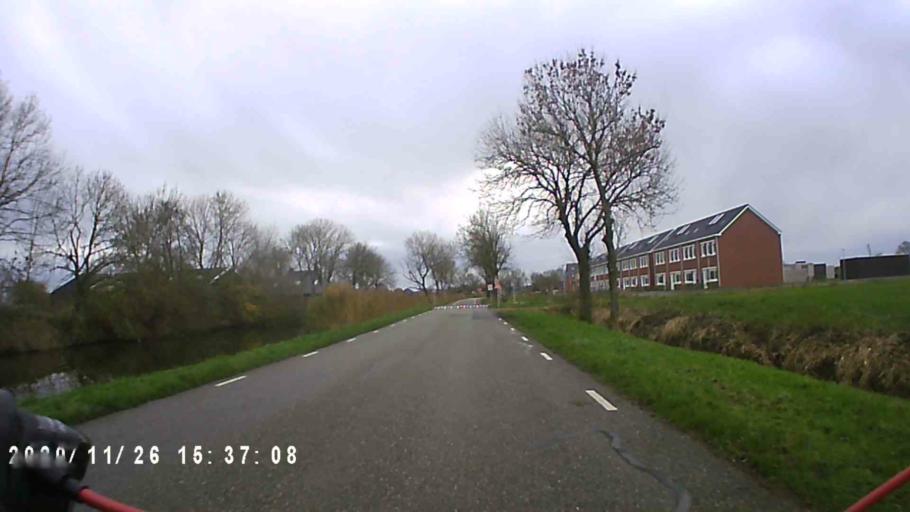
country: NL
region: Groningen
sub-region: Gemeente Slochteren
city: Slochteren
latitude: 53.3019
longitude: 6.7323
